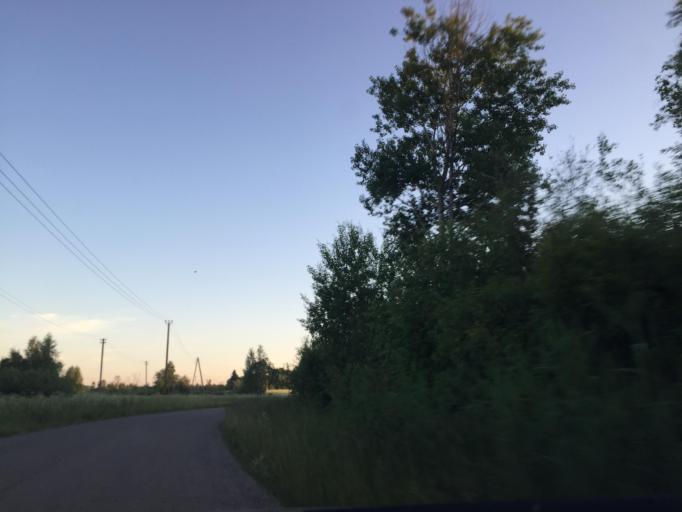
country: LV
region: Rezekne
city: Rezekne
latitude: 56.3773
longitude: 27.4134
